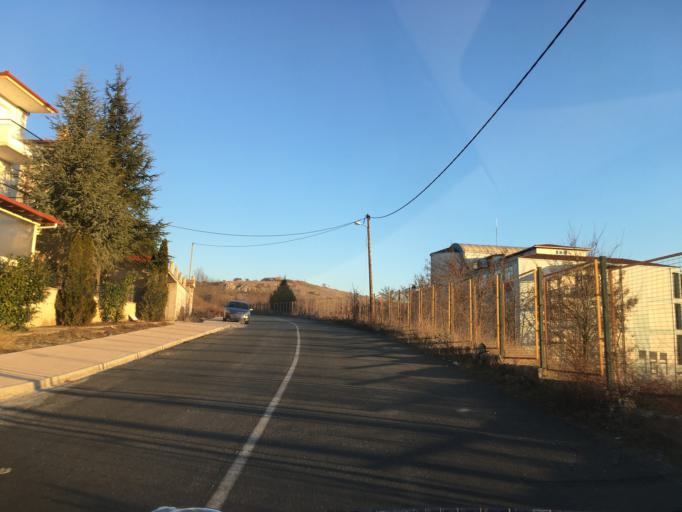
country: GR
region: West Macedonia
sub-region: Nomos Kozanis
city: Koila
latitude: 40.3248
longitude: 21.7926
